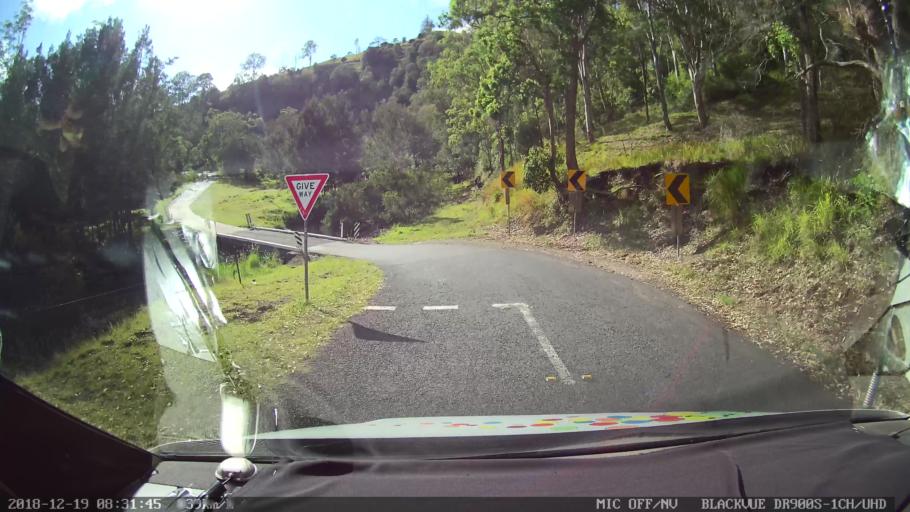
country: AU
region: New South Wales
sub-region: Kyogle
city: Kyogle
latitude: -28.3218
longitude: 152.9394
